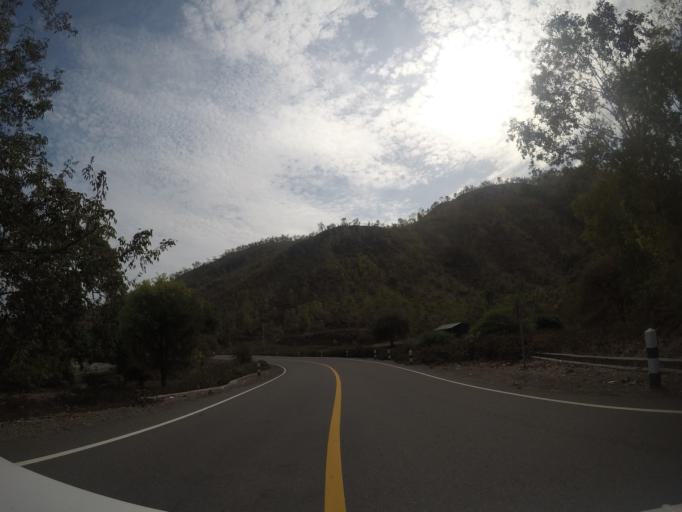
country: ID
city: Metinaro
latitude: -8.5318
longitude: 125.7092
